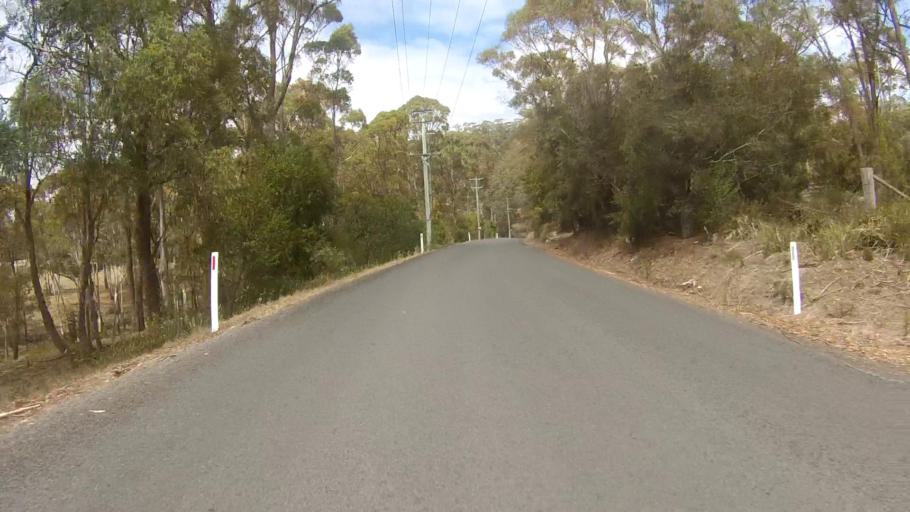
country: AU
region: Tasmania
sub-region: Kingborough
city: Blackmans Bay
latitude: -43.0206
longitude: 147.3219
